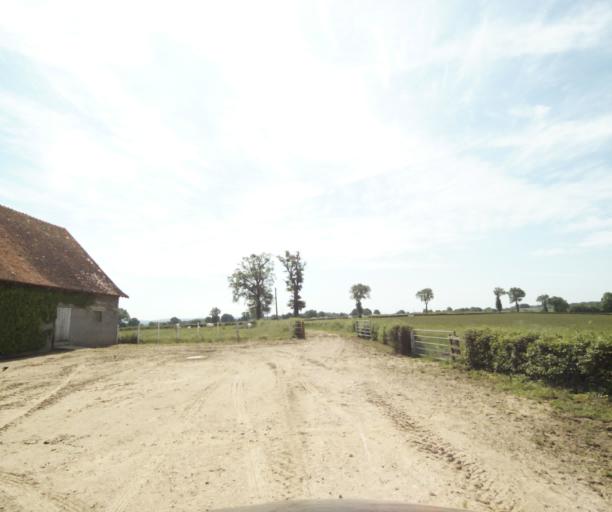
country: FR
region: Bourgogne
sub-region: Departement de Saone-et-Loire
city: Palinges
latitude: 46.5590
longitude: 4.1684
